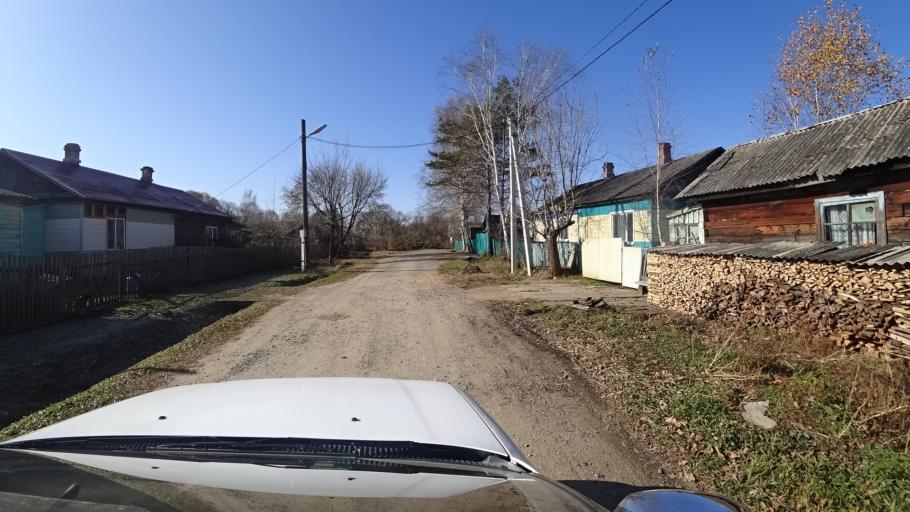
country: RU
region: Primorskiy
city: Dal'nerechensk
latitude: 45.9078
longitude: 133.8050
